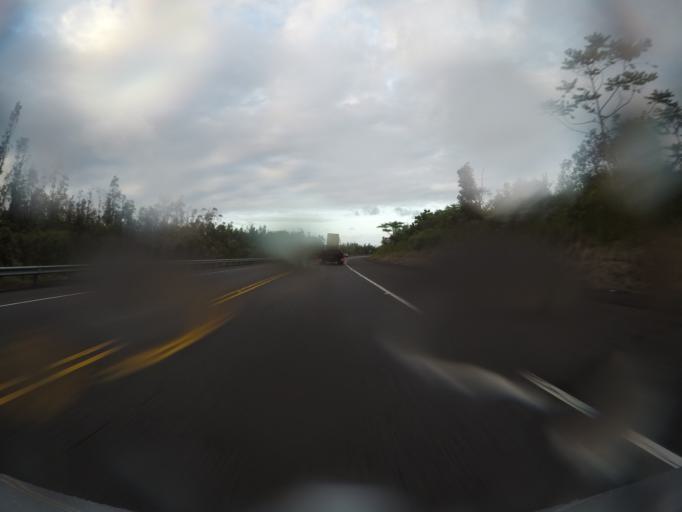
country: US
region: Hawaii
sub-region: Hawaii County
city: Hilo
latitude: 19.6913
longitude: -155.1142
